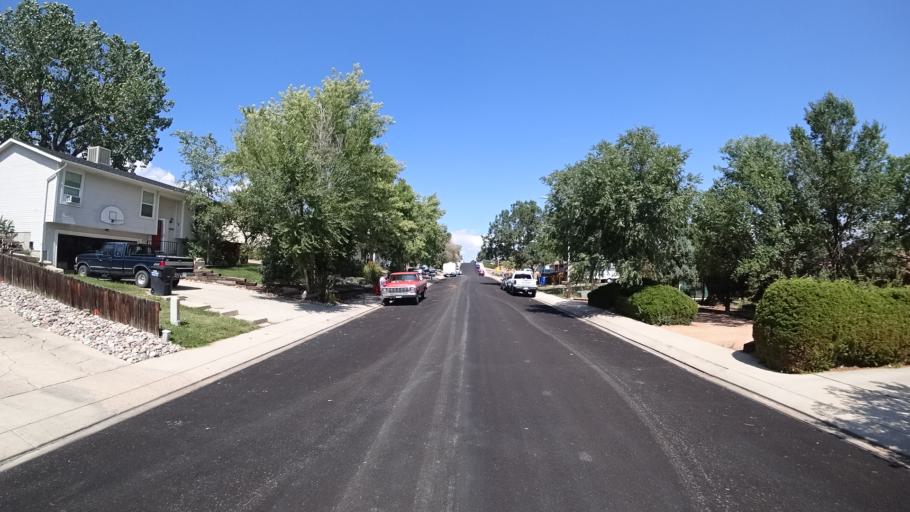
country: US
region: Colorado
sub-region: El Paso County
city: Colorado Springs
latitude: 38.8726
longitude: -104.8397
